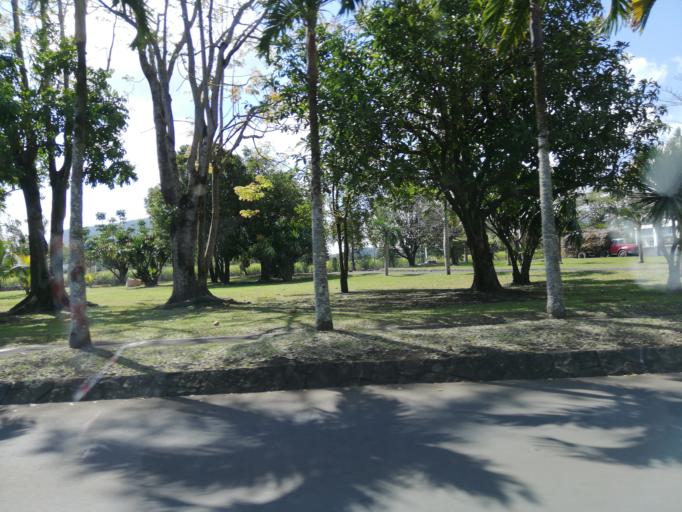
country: MU
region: Moka
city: Verdun
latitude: -20.2239
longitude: 57.5328
